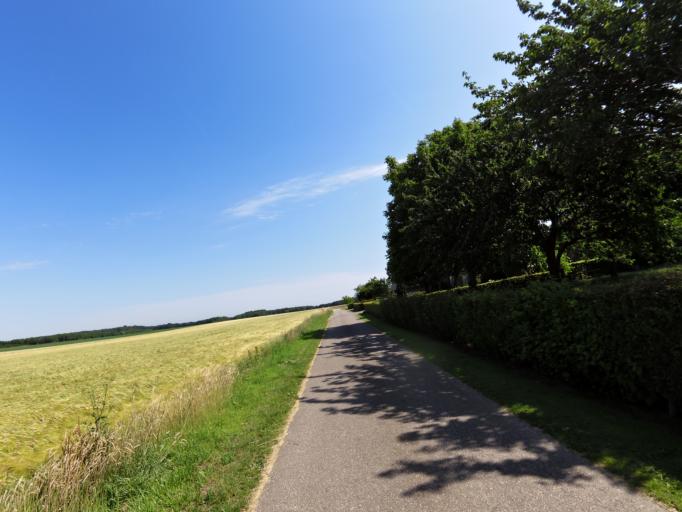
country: NL
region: Limburg
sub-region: Valkenburg aan de Geul
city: Sibbe
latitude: 50.8365
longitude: 5.8375
